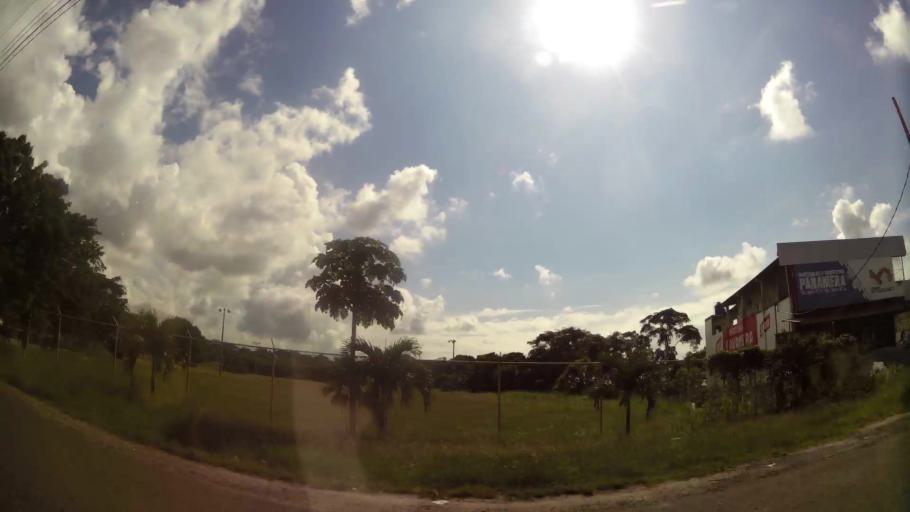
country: PA
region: Panama
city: Nuevo Arraijan
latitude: 8.9091
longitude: -79.7454
